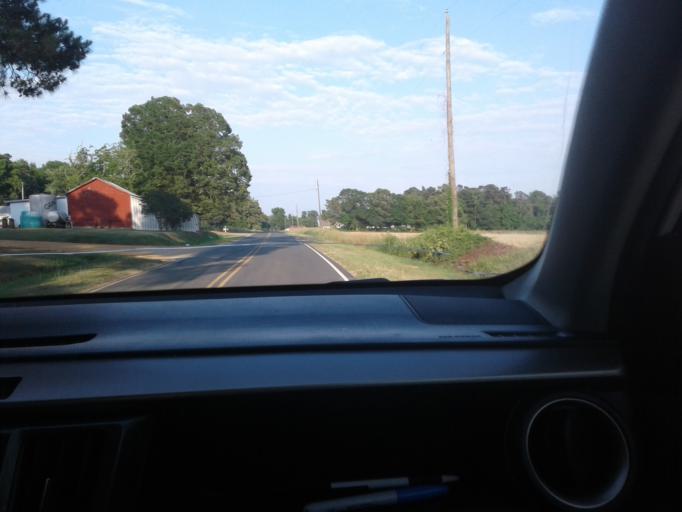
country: US
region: North Carolina
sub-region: Harnett County
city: Dunn
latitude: 35.3348
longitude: -78.5838
